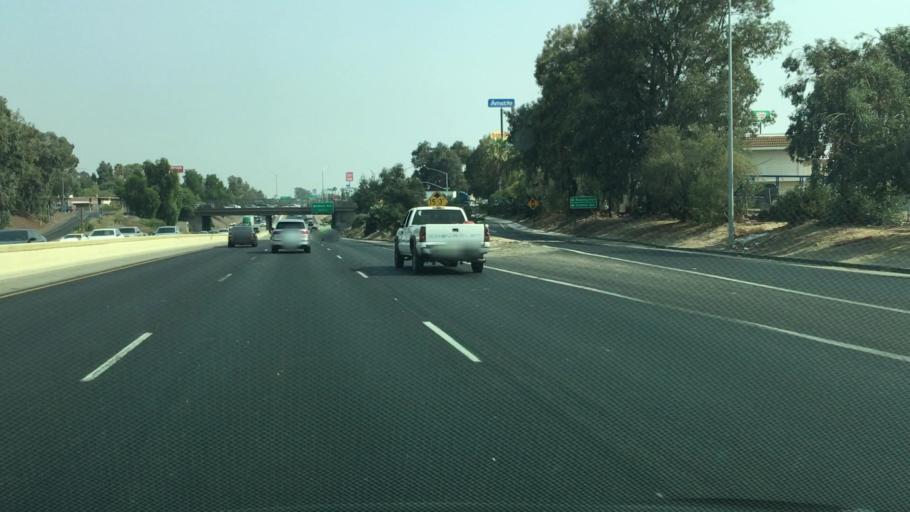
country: US
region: California
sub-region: Fresno County
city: West Park
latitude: 36.7594
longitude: -119.8310
